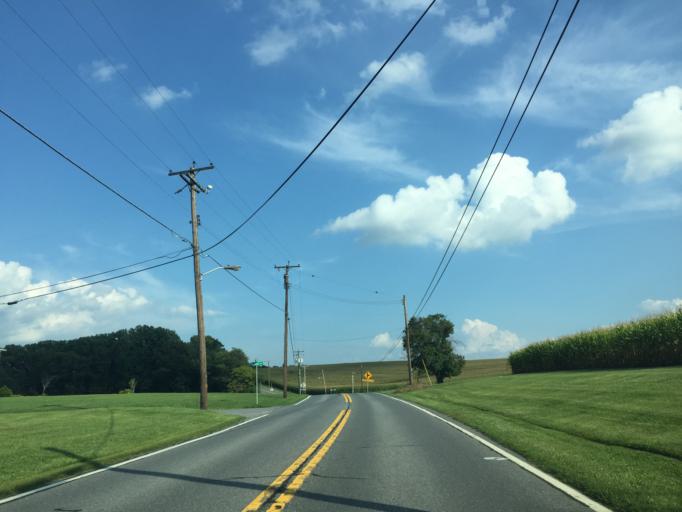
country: US
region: Maryland
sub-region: Carroll County
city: Hampstead
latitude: 39.5946
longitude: -76.7527
